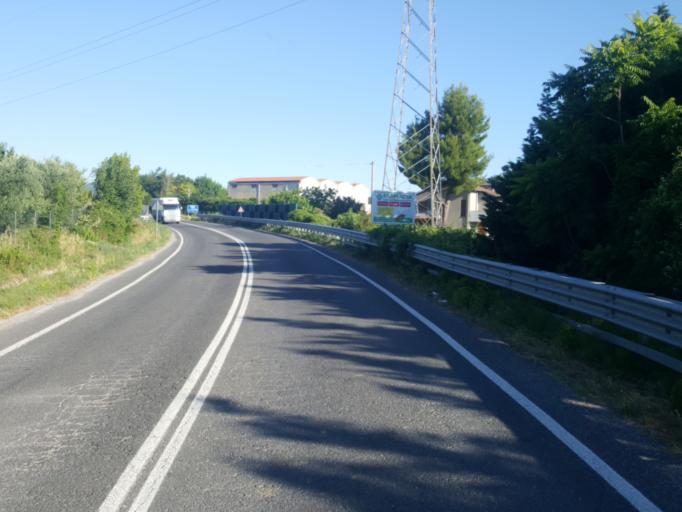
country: IT
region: The Marches
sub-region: Provincia di Pesaro e Urbino
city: Cappone
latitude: 43.8369
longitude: 12.7499
